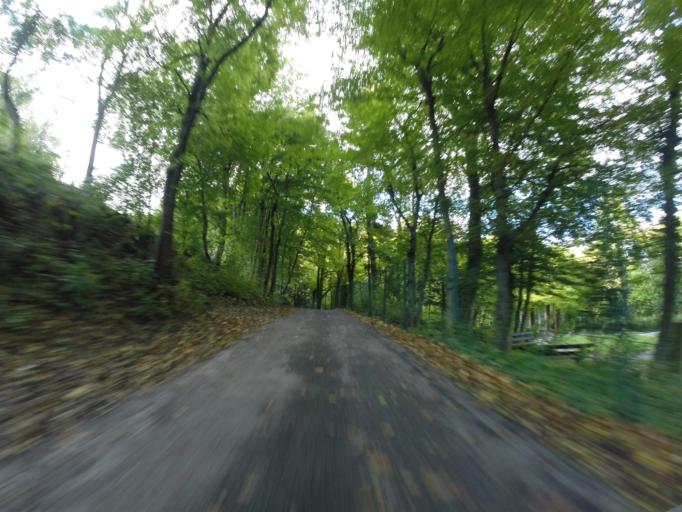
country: DE
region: Thuringia
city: Jena
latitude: 50.9446
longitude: 11.5866
